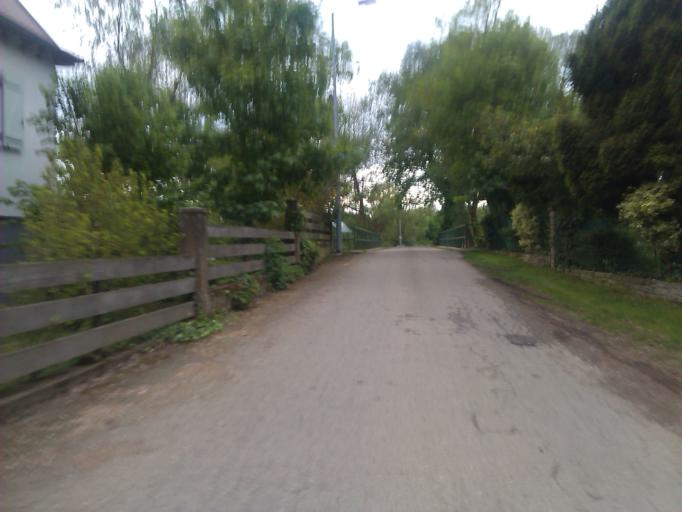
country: FR
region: Alsace
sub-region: Departement du Haut-Rhin
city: Guemar
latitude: 48.1831
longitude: 7.4299
